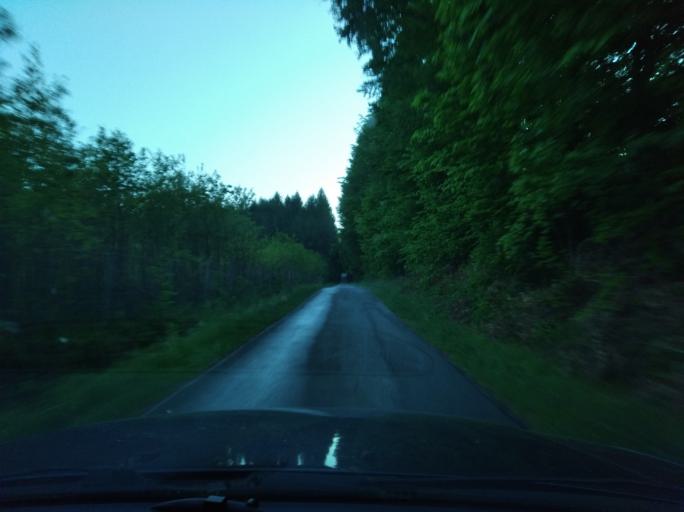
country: PL
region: Subcarpathian Voivodeship
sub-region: Powiat strzyzowski
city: Czudec
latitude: 49.9243
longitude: 21.8436
